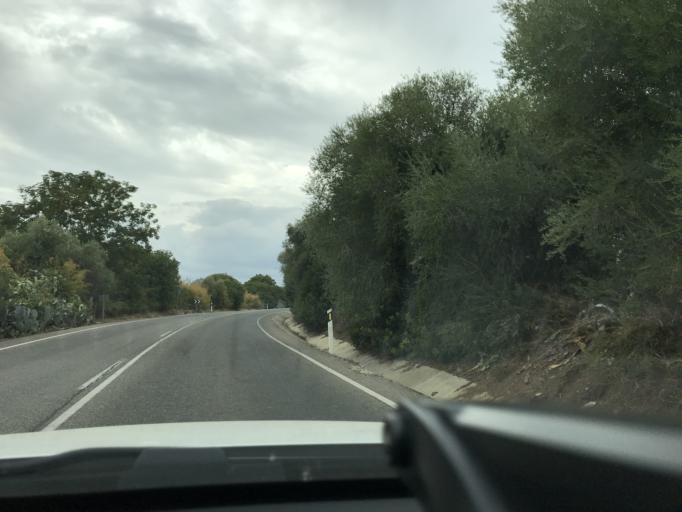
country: ES
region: Andalusia
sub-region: Provincia de Sevilla
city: Villanueva del Rio y Minas
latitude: 37.6346
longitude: -5.7257
